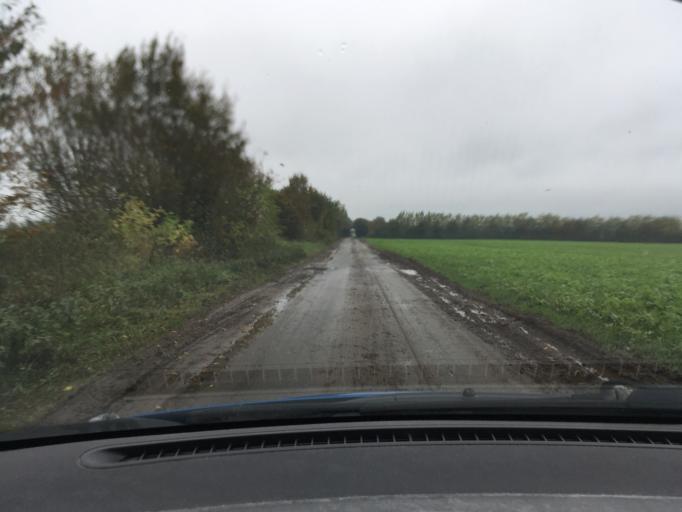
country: DE
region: Schleswig-Holstein
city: Bosau
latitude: 54.1025
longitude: 10.4711
